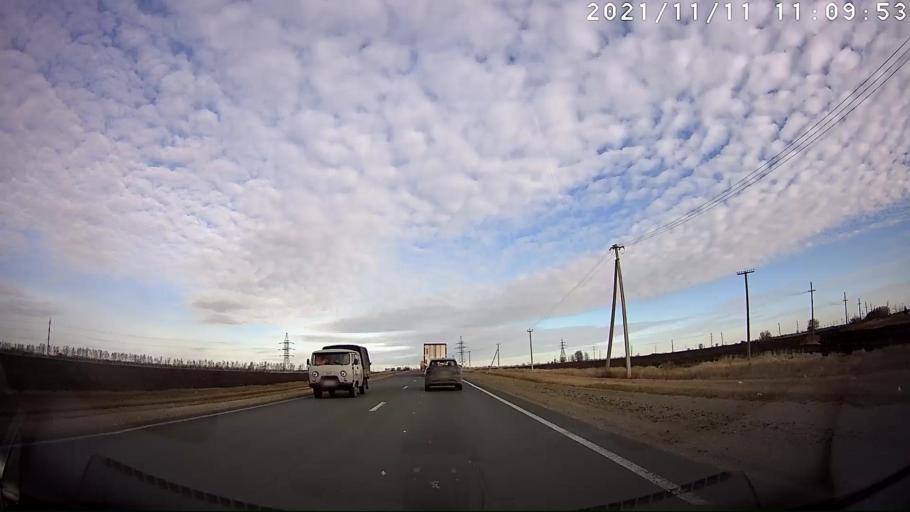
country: RU
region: Samara
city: Varlamovo
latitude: 53.1830
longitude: 48.2886
